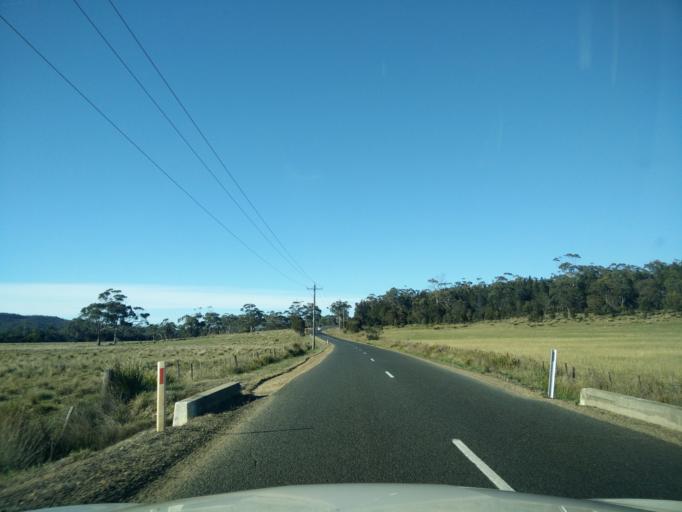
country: AU
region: Tasmania
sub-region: Break O'Day
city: St Helens
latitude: -41.9134
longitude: 148.2496
